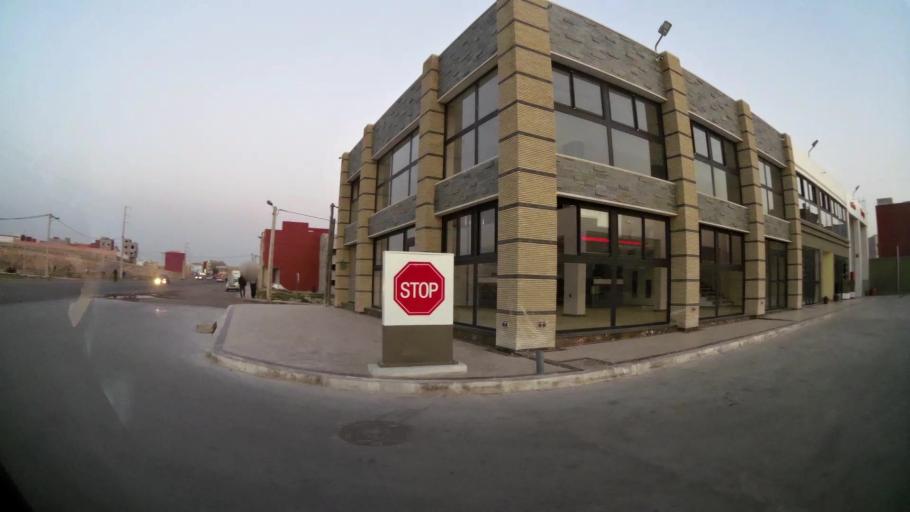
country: MA
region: Souss-Massa-Draa
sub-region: Inezgane-Ait Mellou
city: Inezgane
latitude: 30.3758
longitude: -9.4872
